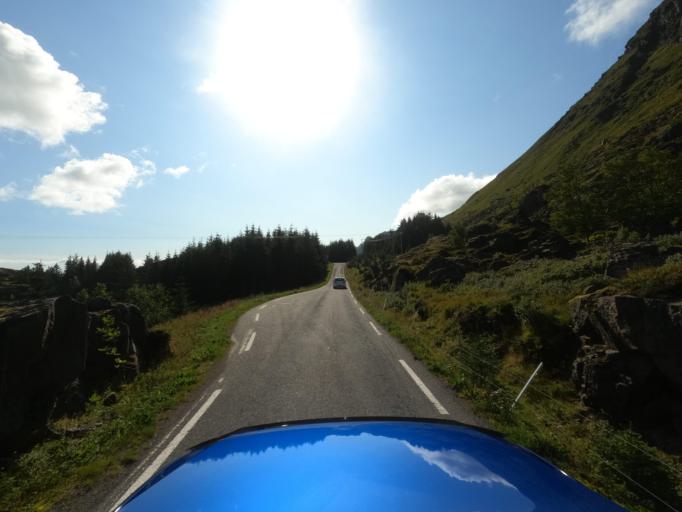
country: NO
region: Nordland
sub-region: Vestvagoy
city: Leknes
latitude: 68.1246
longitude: 13.7406
